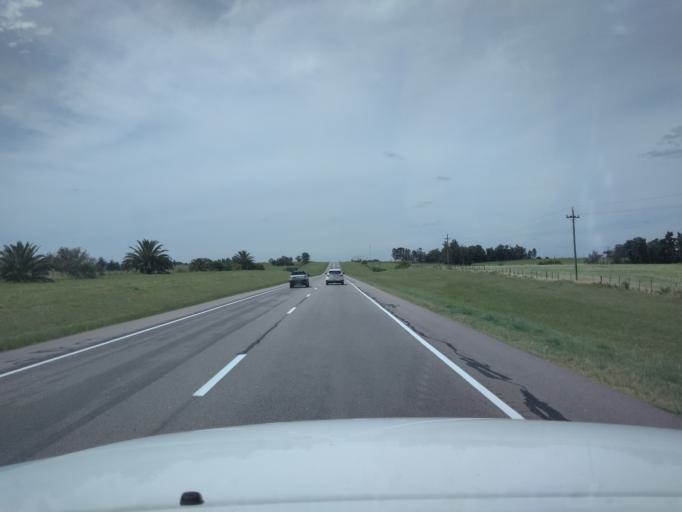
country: UY
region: Florida
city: Florida
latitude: -34.2196
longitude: -56.2086
